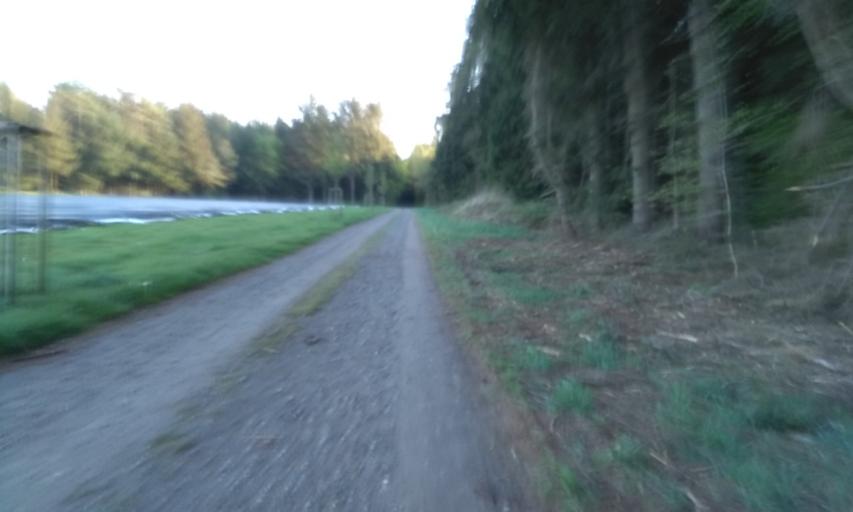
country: DE
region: Lower Saxony
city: Dollern
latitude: 53.5259
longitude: 9.5412
